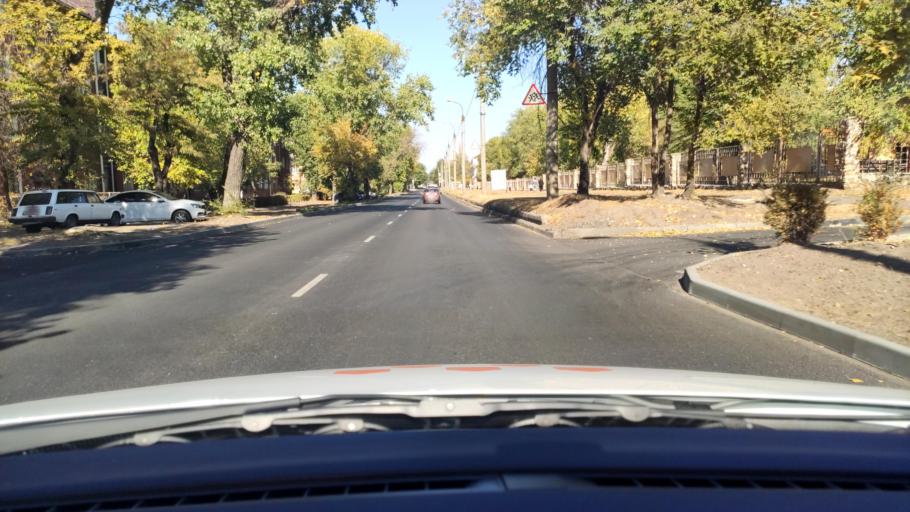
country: RU
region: Voronezj
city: Voronezh
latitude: 51.6401
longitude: 39.2400
